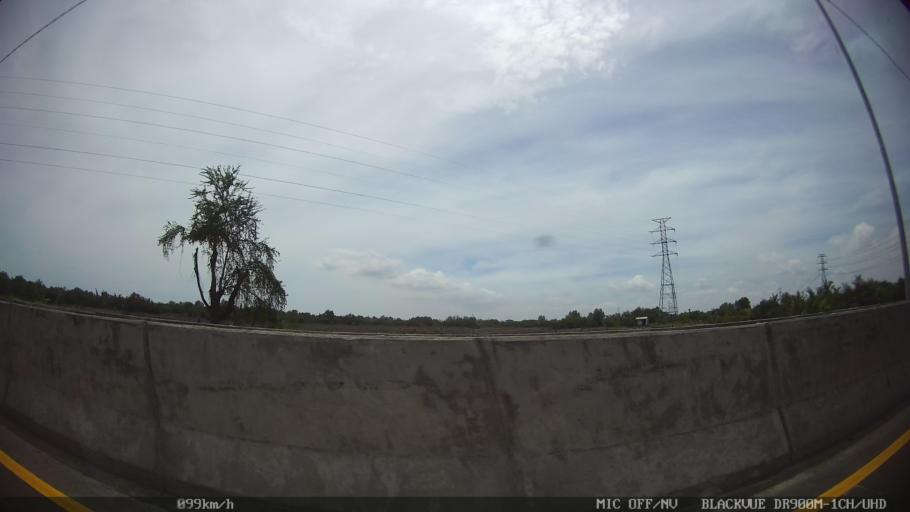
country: ID
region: North Sumatra
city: Labuhan Deli
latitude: 3.7481
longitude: 98.6808
